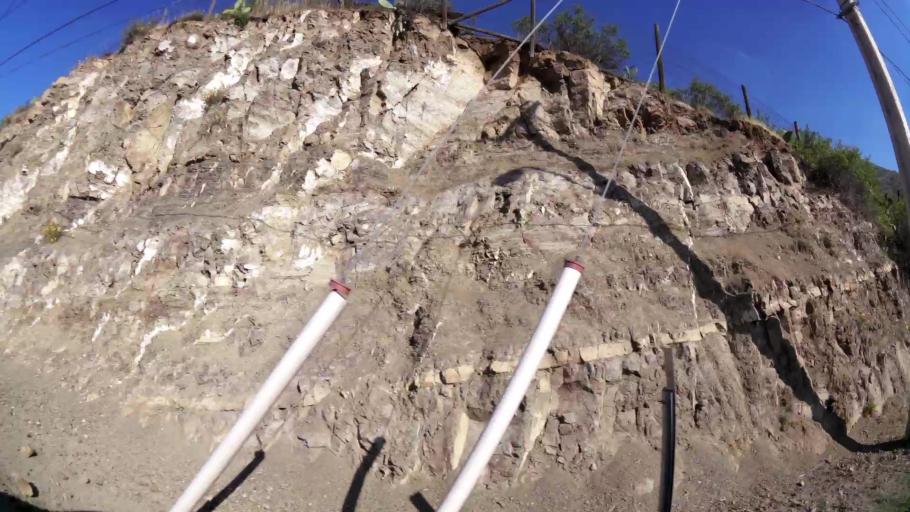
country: CL
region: Santiago Metropolitan
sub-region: Provincia de Santiago
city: Villa Presidente Frei, Nunoa, Santiago, Chile
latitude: -33.3645
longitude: -70.4819
